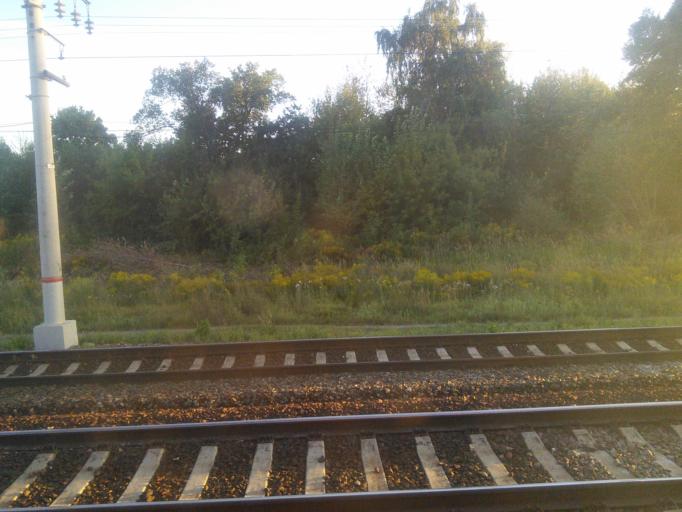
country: RU
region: Moskovskaya
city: Kupavna
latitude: 55.7510
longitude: 38.1301
